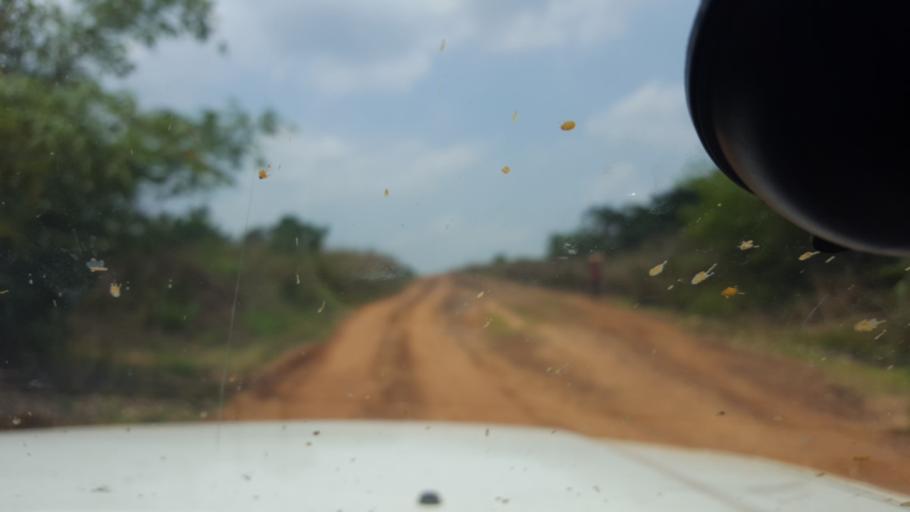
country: CD
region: Bandundu
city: Mushie
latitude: -3.7486
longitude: 16.6599
